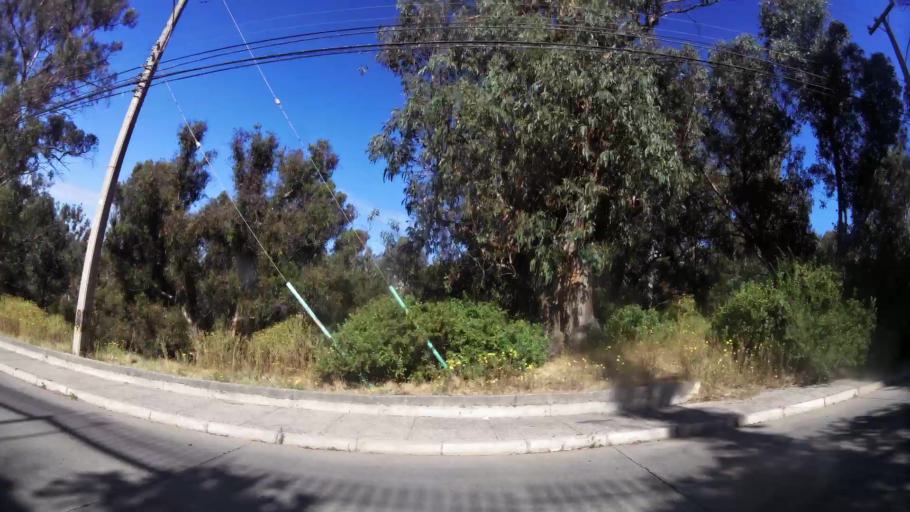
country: CL
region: Valparaiso
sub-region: Provincia de Valparaiso
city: Vina del Mar
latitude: -33.0363
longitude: -71.5625
